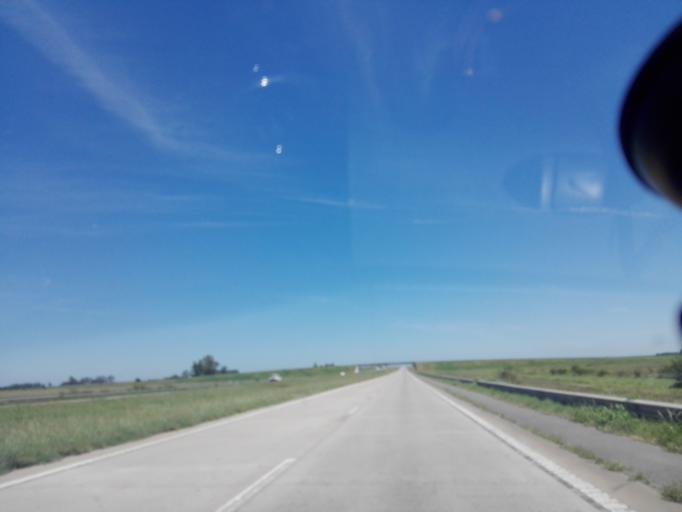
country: AR
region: Santa Fe
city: Canada de Gomez
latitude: -32.8415
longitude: -61.4267
